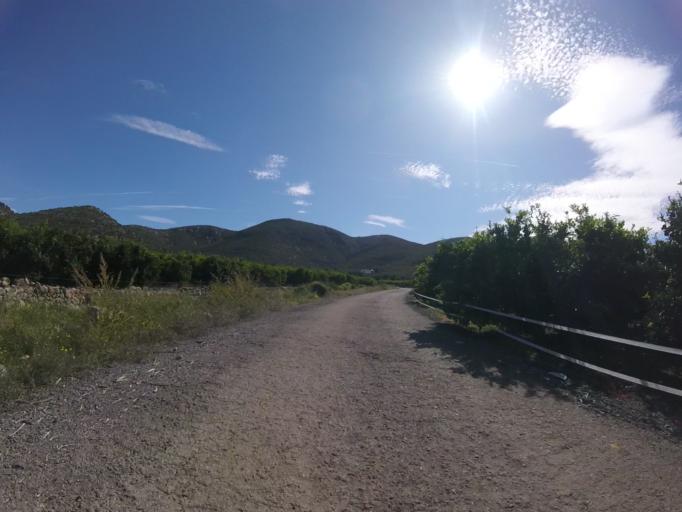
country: ES
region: Valencia
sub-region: Provincia de Castello
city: Santa Magdalena de Pulpis
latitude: 40.3797
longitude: 0.3375
